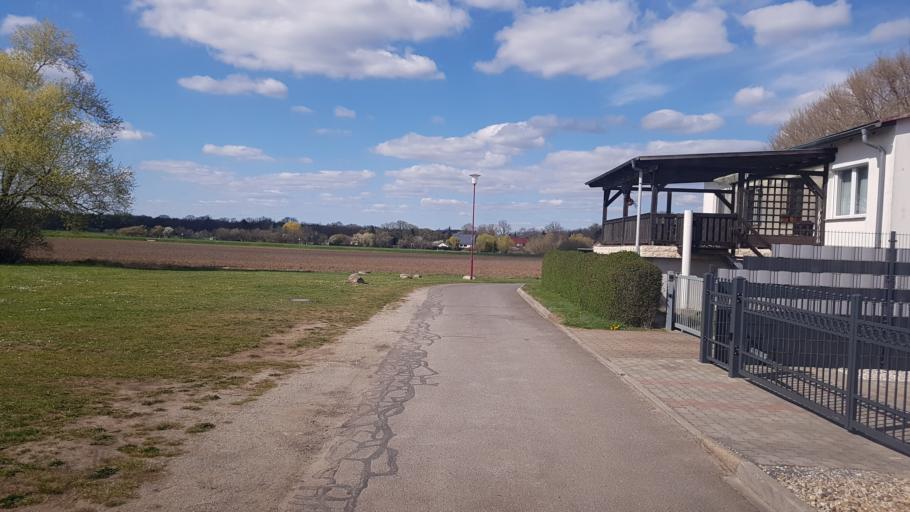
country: DE
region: Brandenburg
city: Sonnewalde
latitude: 51.6904
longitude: 13.6428
